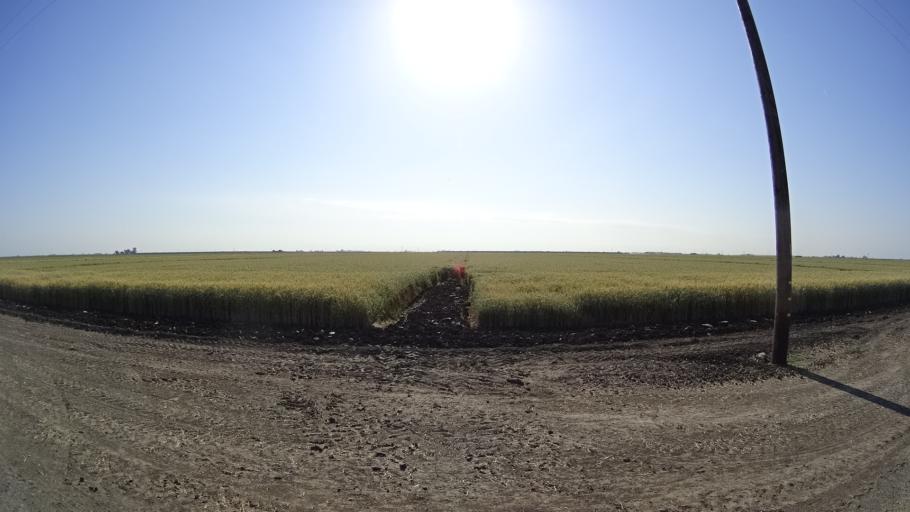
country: US
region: California
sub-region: Kings County
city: Home Garden
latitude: 36.2614
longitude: -119.5294
